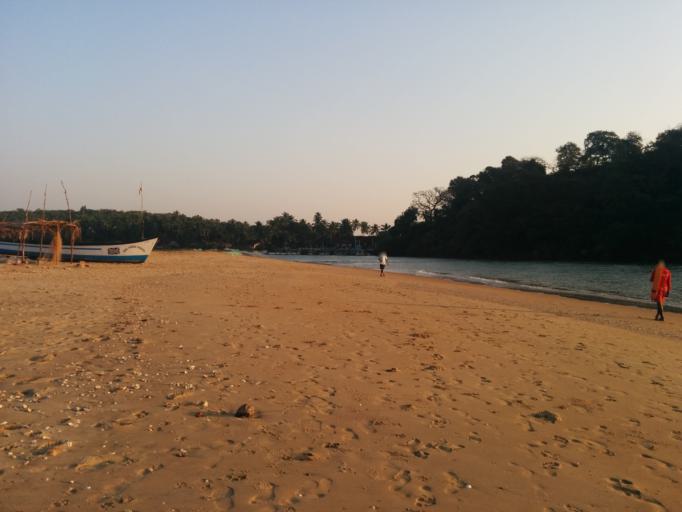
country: IN
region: Karnataka
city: Canacona
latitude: 14.9854
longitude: 74.0384
